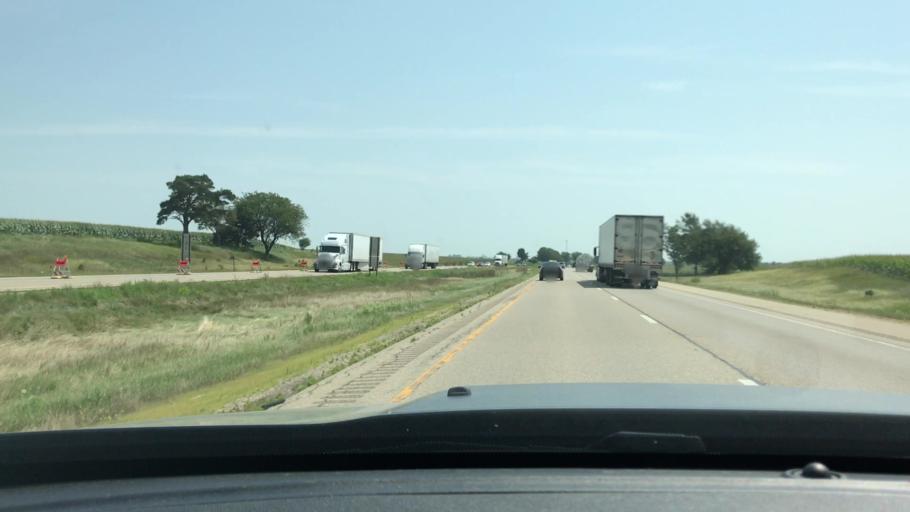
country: US
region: Illinois
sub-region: Bureau County
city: Depue
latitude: 41.4002
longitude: -89.3228
